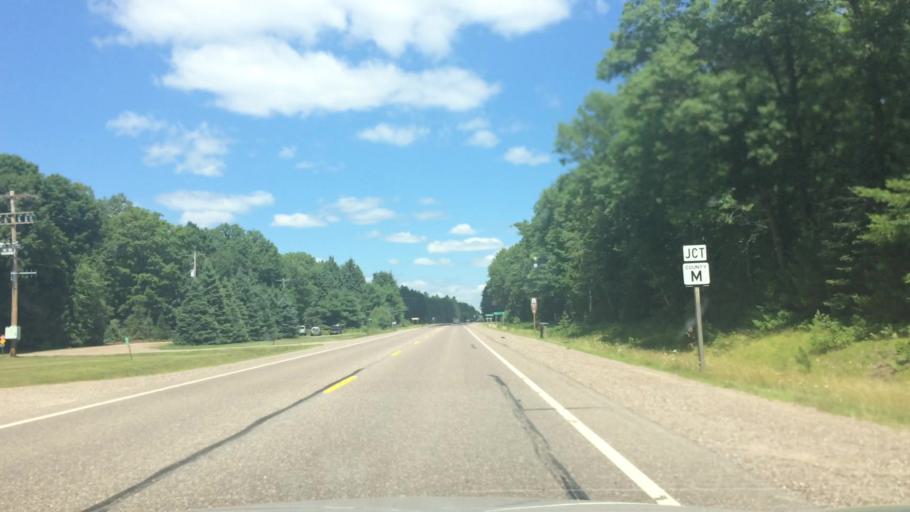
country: US
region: Wisconsin
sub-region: Vilas County
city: Lac du Flambeau
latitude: 45.9788
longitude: -89.6990
